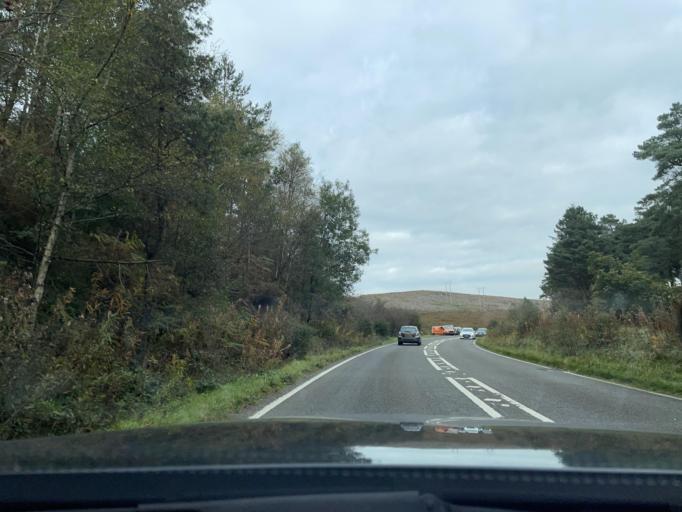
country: GB
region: England
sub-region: Derbyshire
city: Hathersage
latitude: 53.3820
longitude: -1.6817
